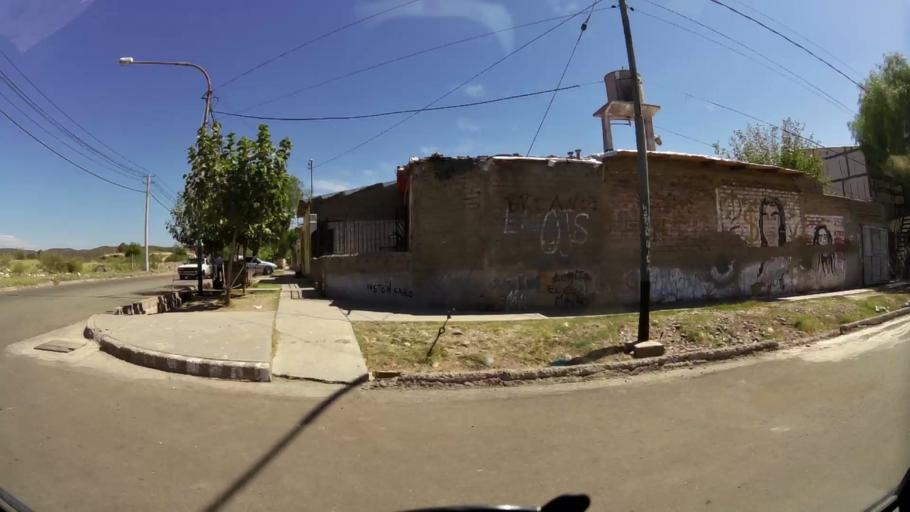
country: AR
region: Mendoza
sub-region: Departamento de Godoy Cruz
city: Godoy Cruz
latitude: -32.9492
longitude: -68.8691
